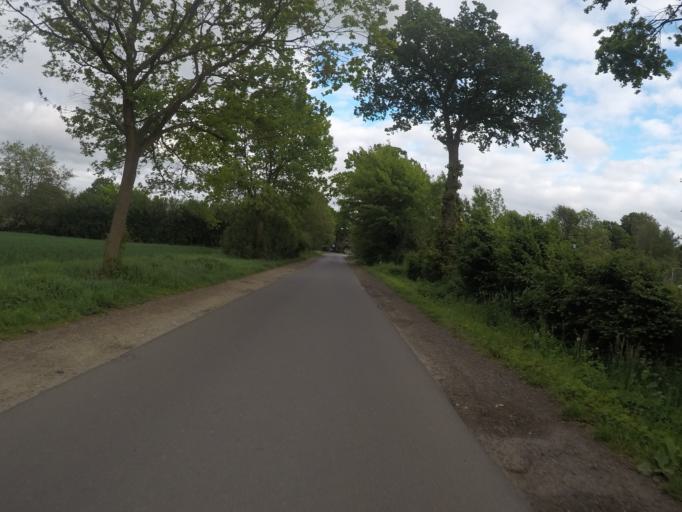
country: DE
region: Schleswig-Holstein
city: Hasloh
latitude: 53.7002
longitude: 9.9225
